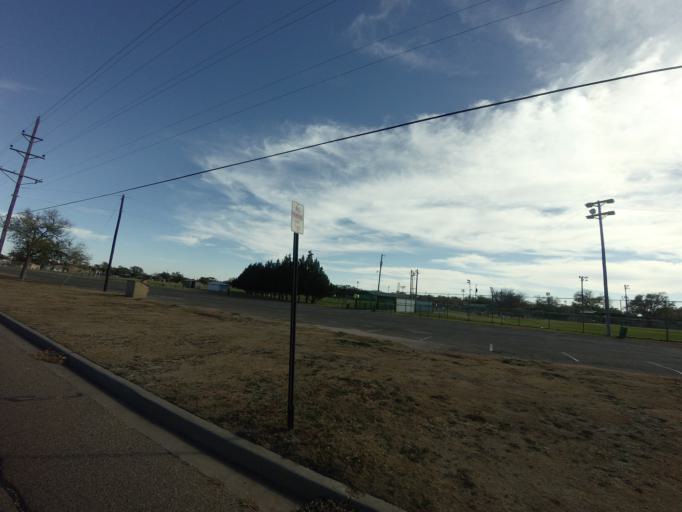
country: US
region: New Mexico
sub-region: Curry County
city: Clovis
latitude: 34.4120
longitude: -103.1824
